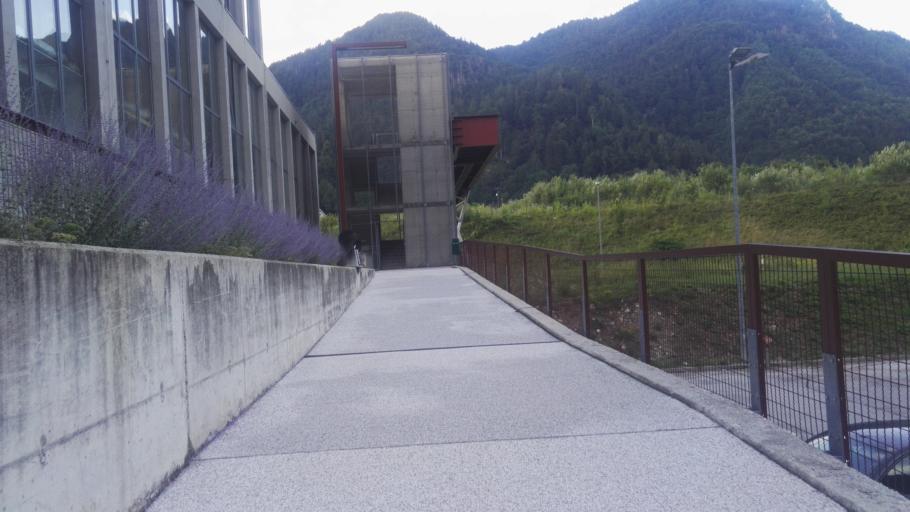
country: SI
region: Jesenice
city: Jesenice
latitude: 46.4333
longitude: 14.0582
